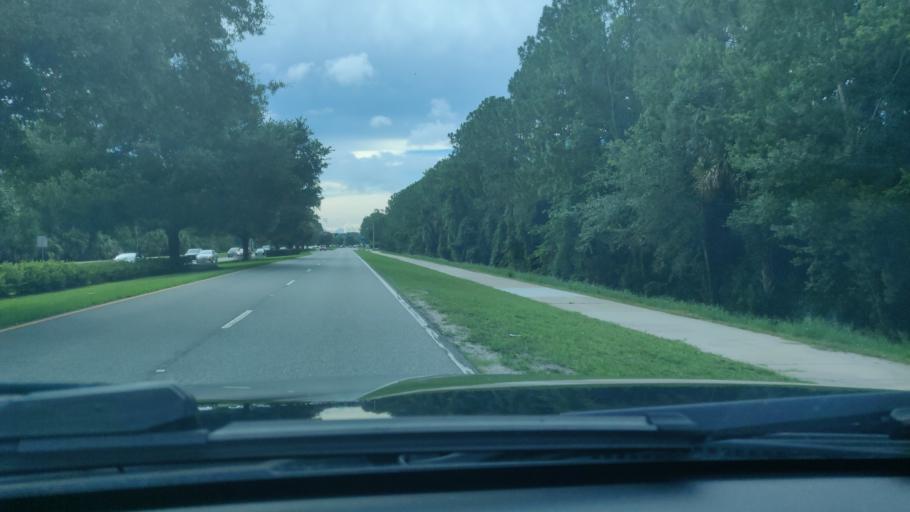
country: US
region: Florida
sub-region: Flagler County
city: Palm Coast
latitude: 29.5442
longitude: -81.2310
